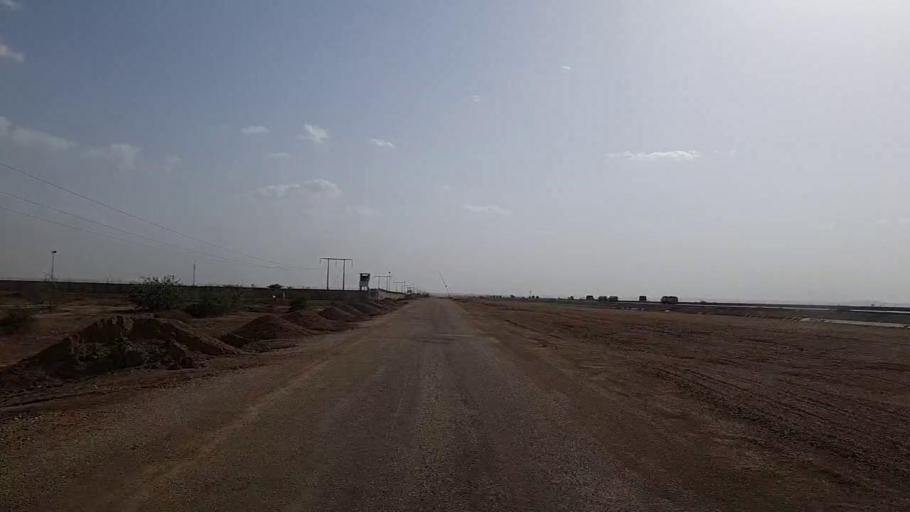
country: PK
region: Sindh
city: Kotri
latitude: 25.2894
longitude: 68.0469
